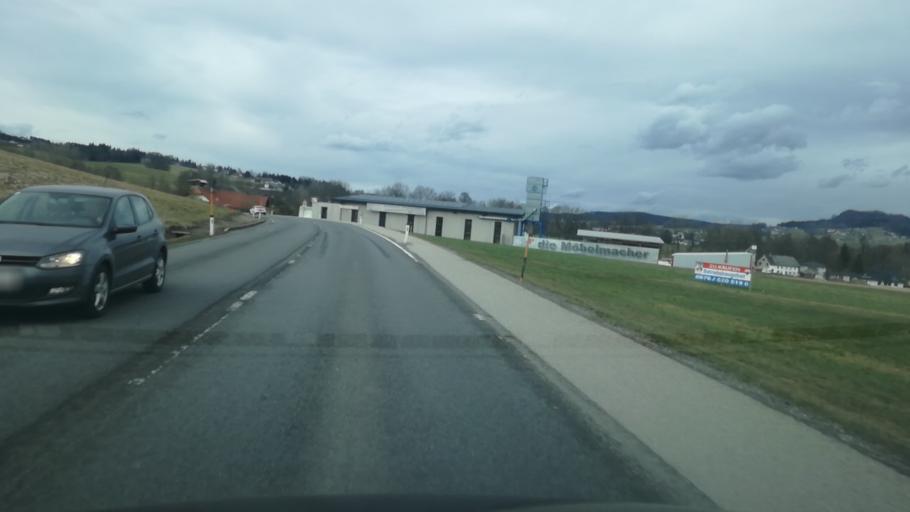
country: AT
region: Upper Austria
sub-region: Politischer Bezirk Vocklabruck
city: Frankenburg
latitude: 48.0491
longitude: 13.4855
